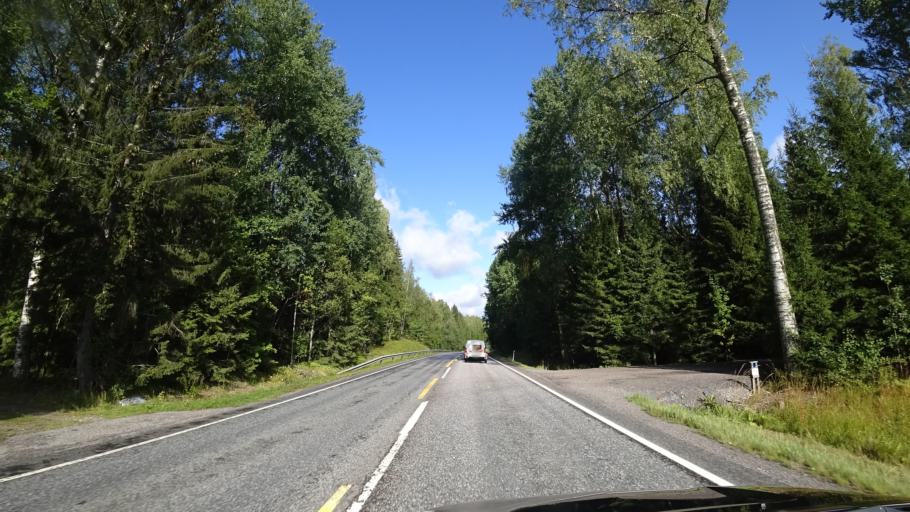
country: FI
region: Uusimaa
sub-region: Helsinki
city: Tuusula
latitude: 60.4487
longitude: 24.9620
